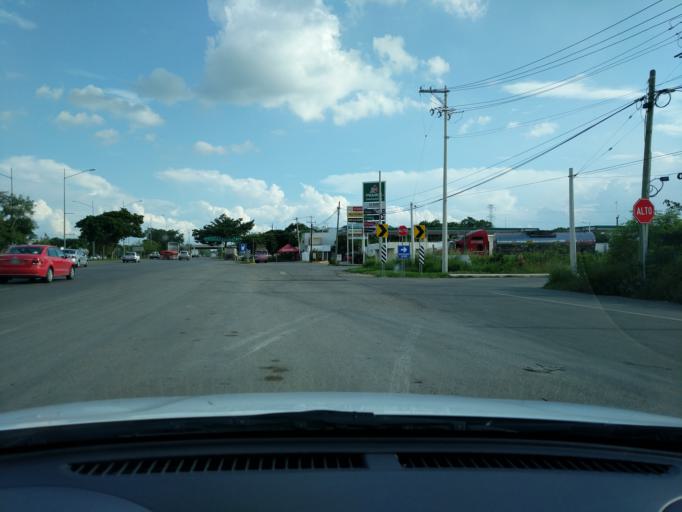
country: MX
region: Yucatan
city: Itzincab Palomeque
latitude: 20.9053
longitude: -89.6774
